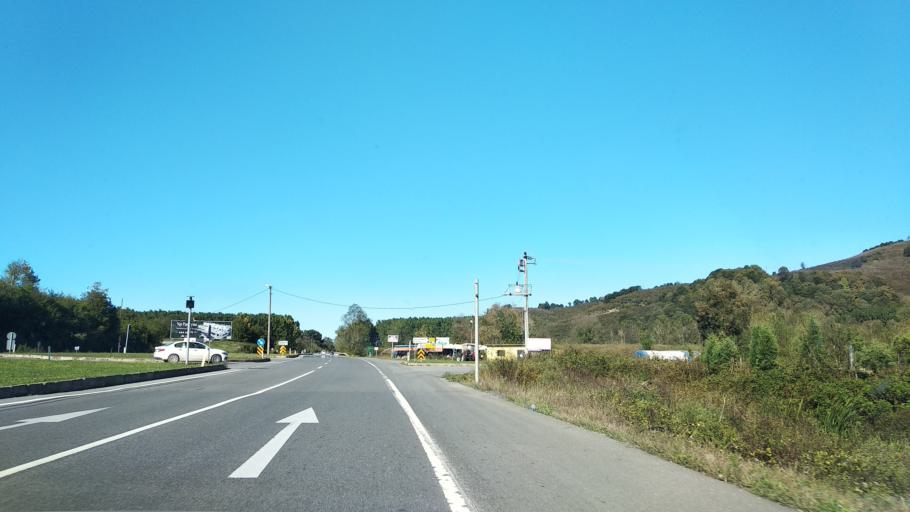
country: TR
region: Sakarya
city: Karasu
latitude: 41.0538
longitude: 30.6355
